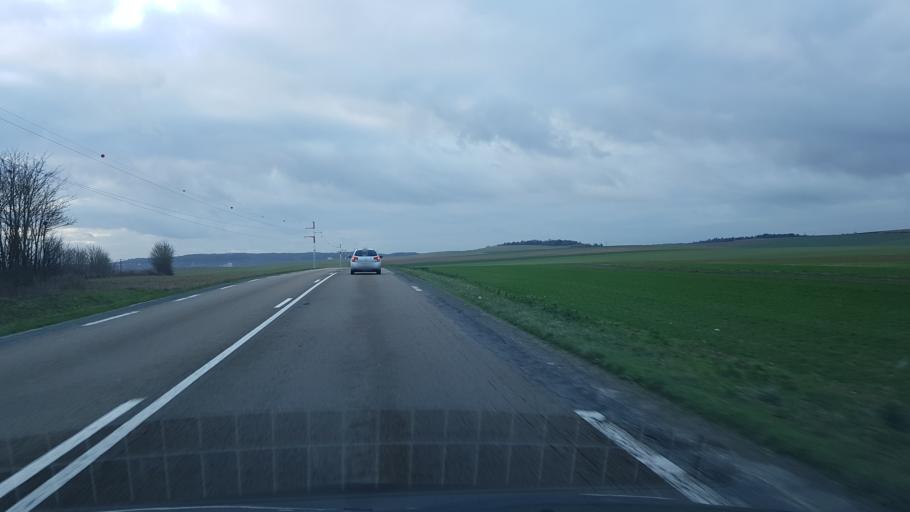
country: FR
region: Champagne-Ardenne
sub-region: Departement de la Marne
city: Sezanne
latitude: 48.7208
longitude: 3.7778
